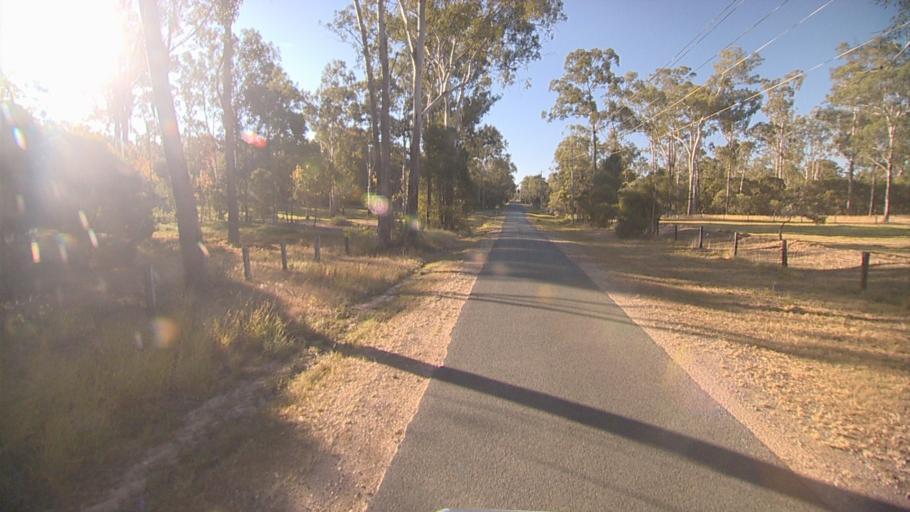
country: AU
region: Queensland
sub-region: Logan
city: North Maclean
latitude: -27.7846
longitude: 153.0458
